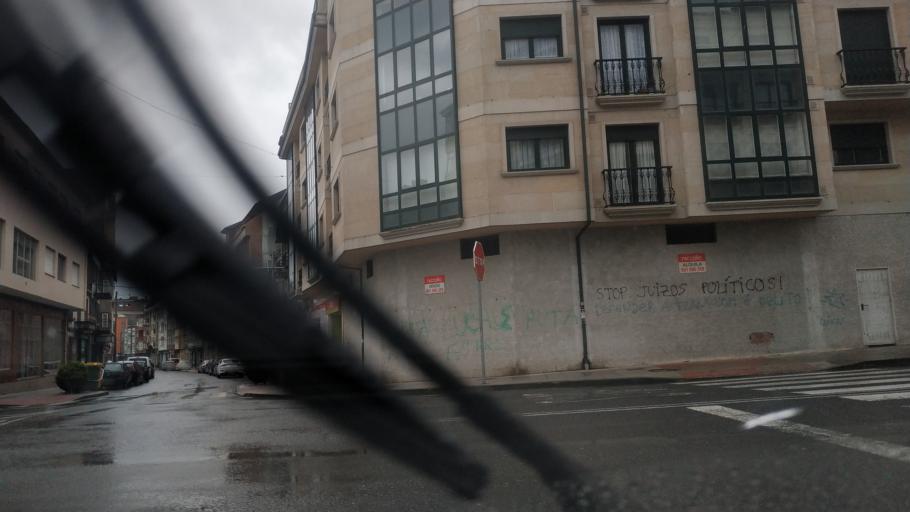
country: ES
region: Galicia
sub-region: Provincia da Coruna
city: Negreira
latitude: 42.9118
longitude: -8.7368
